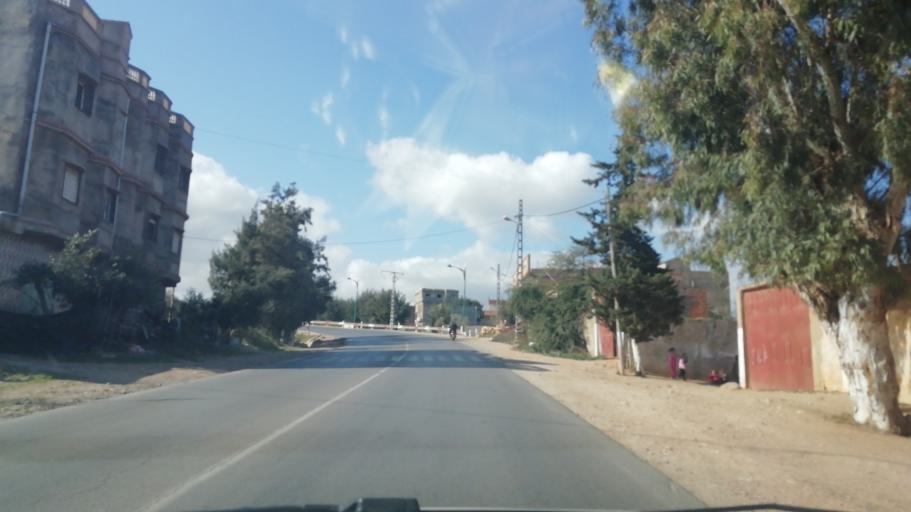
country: DZ
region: Relizane
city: Mazouna
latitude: 36.2853
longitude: 0.6450
